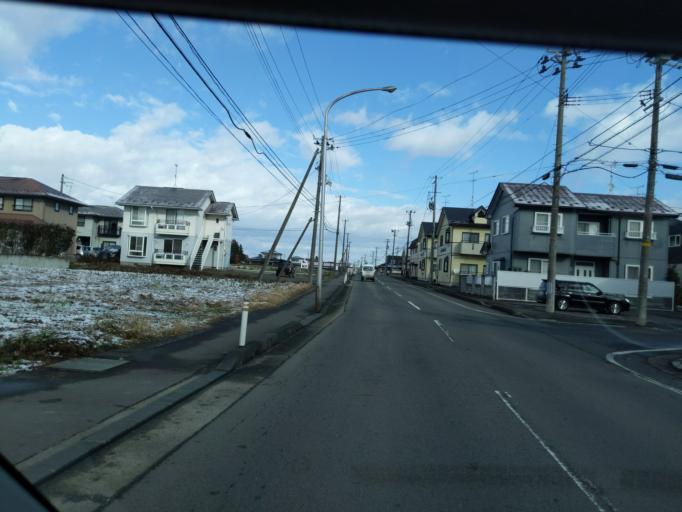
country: JP
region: Iwate
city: Mizusawa
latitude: 39.1119
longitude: 141.1369
